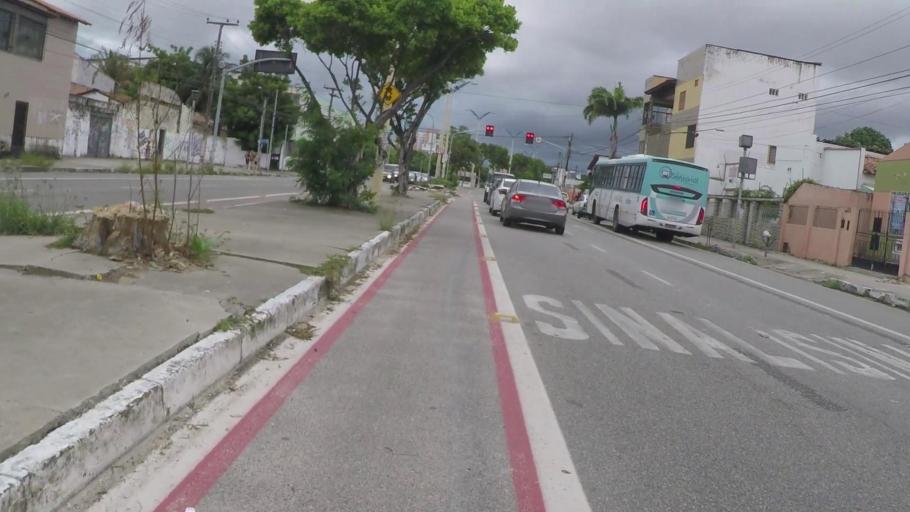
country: BR
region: Ceara
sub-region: Fortaleza
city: Fortaleza
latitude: -3.7336
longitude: -38.5405
